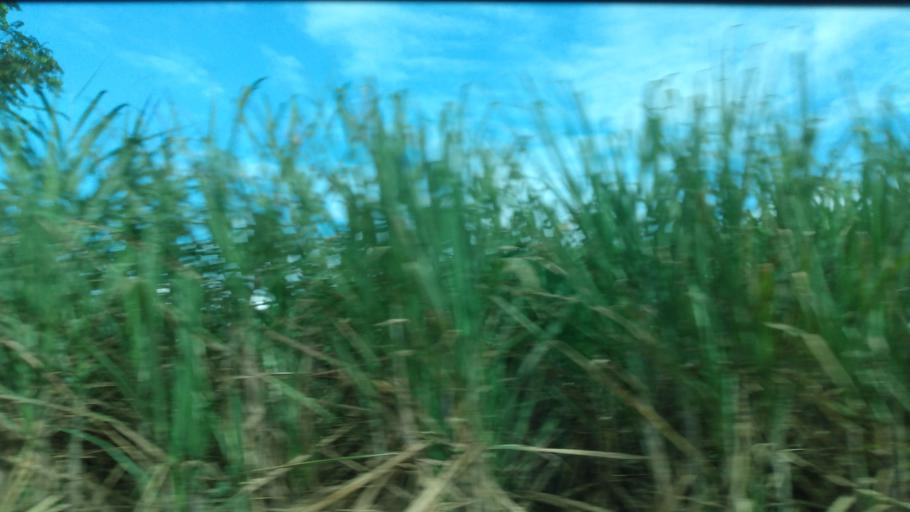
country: BR
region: Pernambuco
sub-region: Palmares
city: Palmares
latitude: -8.6946
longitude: -35.6470
